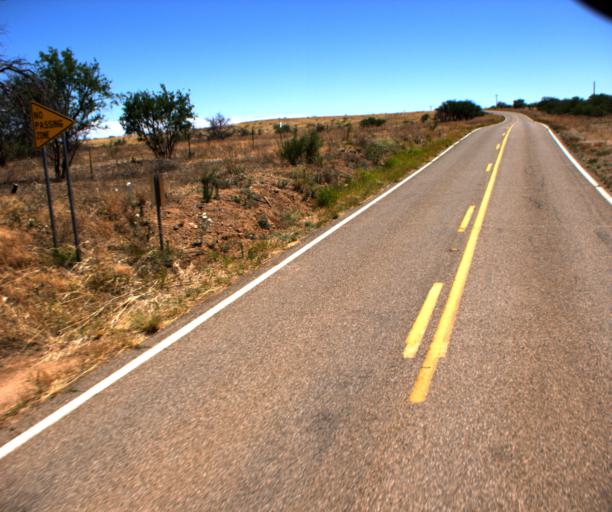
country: US
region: Arizona
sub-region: Pima County
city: Sells
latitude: 31.5811
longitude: -111.5360
